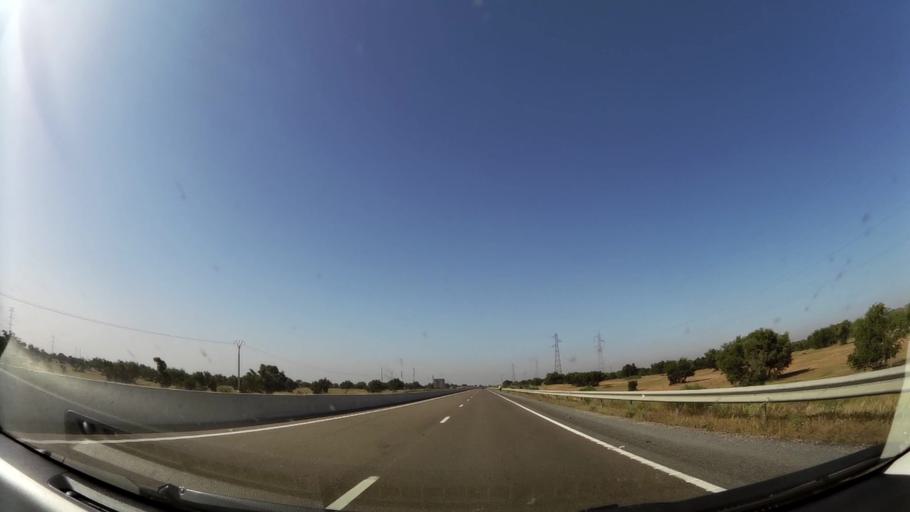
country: MA
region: Souss-Massa-Draa
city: Oulad Teima
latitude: 30.4391
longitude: -9.3691
